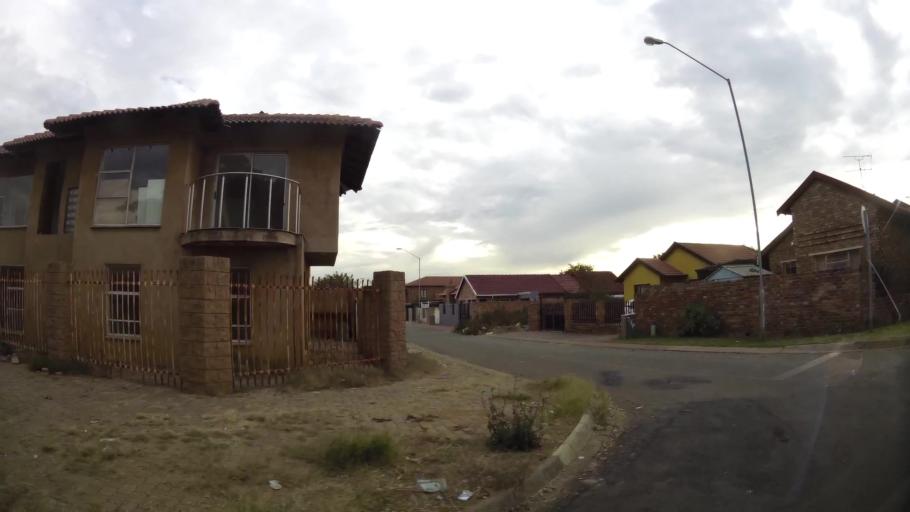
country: ZA
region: Gauteng
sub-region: City of Tshwane Metropolitan Municipality
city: Pretoria
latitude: -25.7047
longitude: 28.3083
